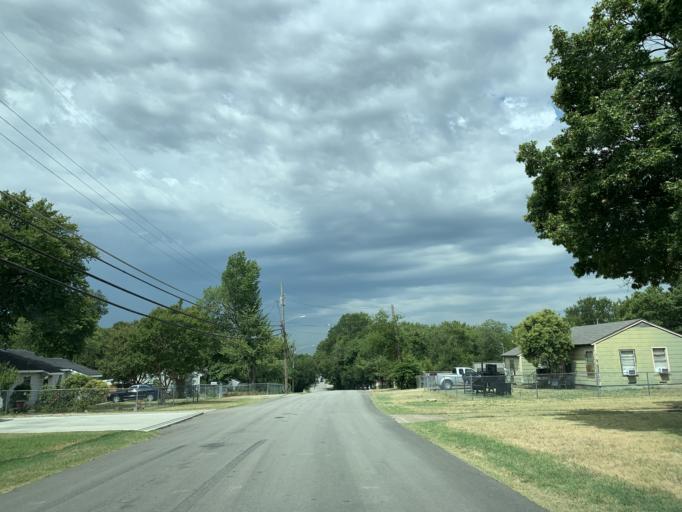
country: US
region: Texas
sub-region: Dallas County
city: Duncanville
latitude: 32.6724
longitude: -96.8312
